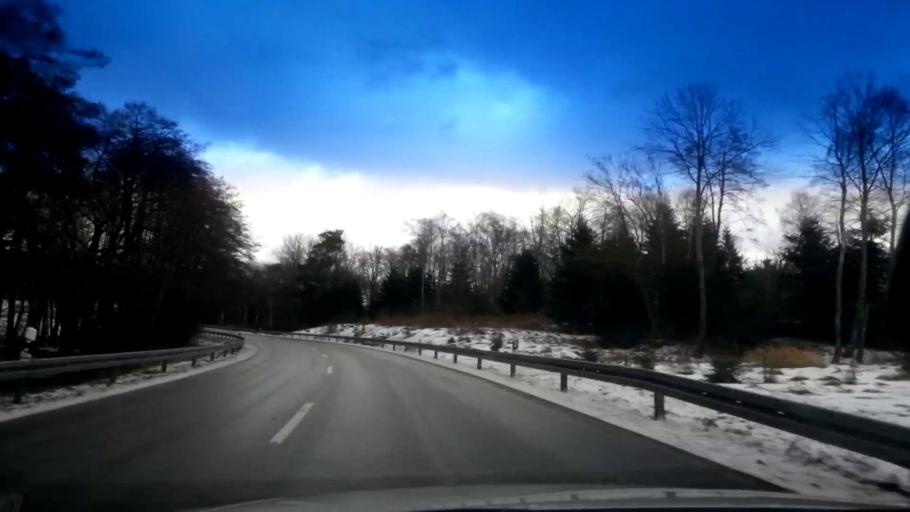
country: DE
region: Bavaria
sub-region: Upper Franconia
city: Weissenstadt
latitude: 50.1181
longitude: 11.9032
